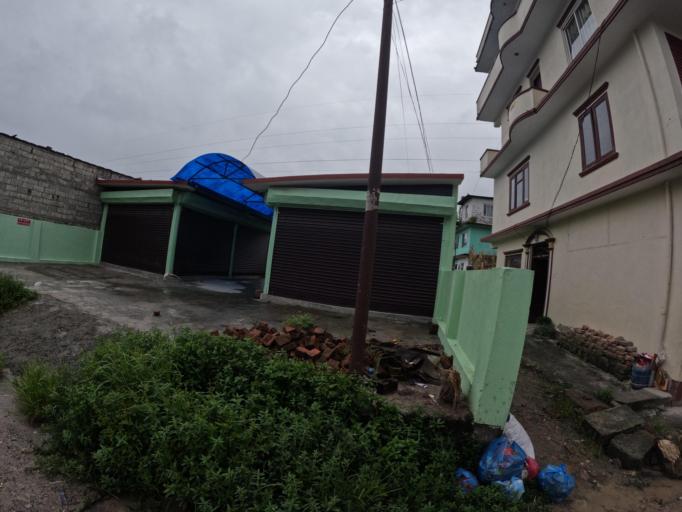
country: NP
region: Central Region
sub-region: Bagmati Zone
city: Kathmandu
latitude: 27.7635
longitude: 85.3207
